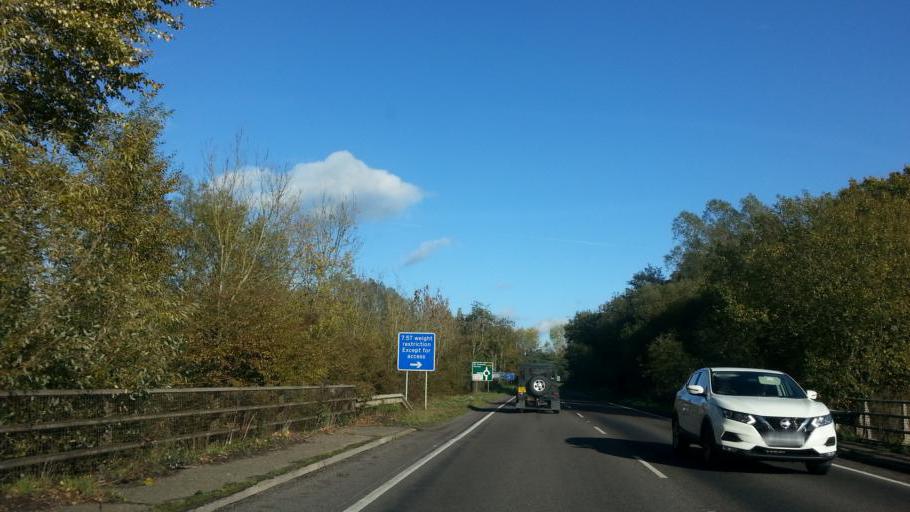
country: GB
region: England
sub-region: Norfolk
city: Ditchingham
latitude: 52.4626
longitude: 1.4391
